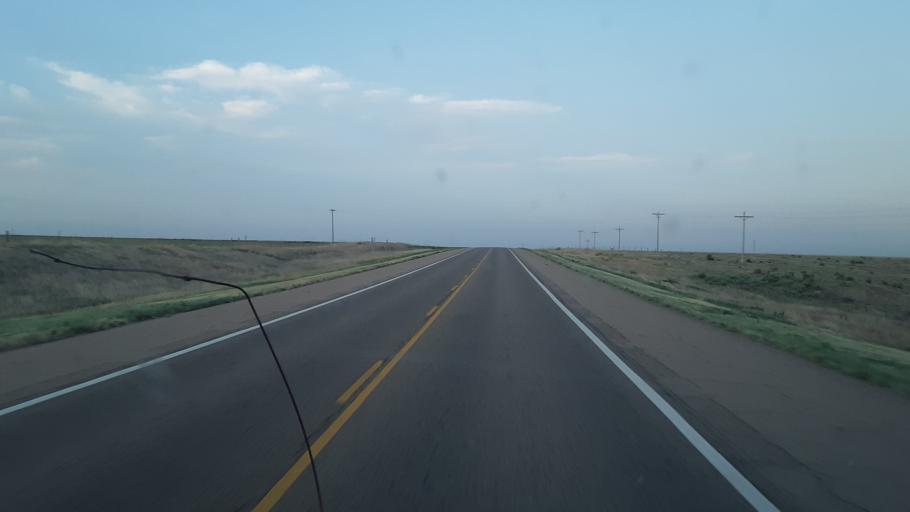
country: US
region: Kansas
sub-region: Kearny County
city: Lakin
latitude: 37.9440
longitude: -101.4436
